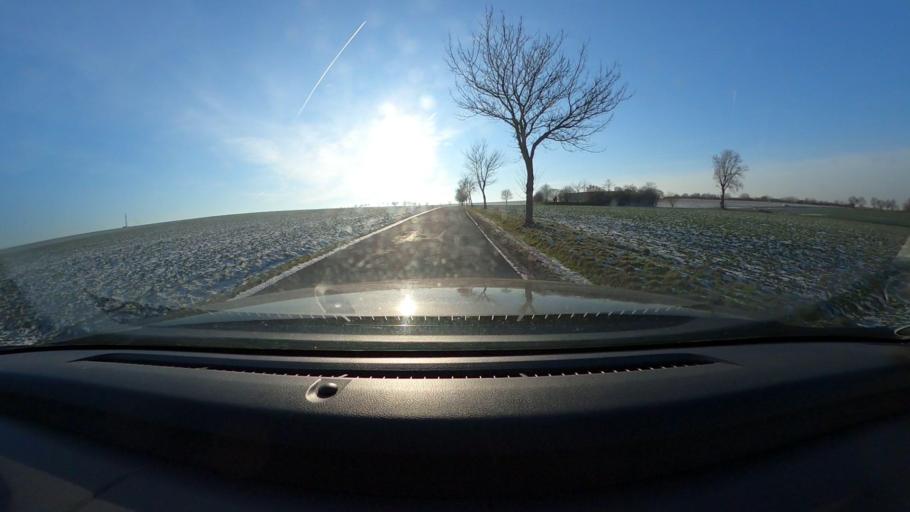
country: DE
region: Saxony
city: Frankenstein
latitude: 50.9517
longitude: 13.2309
